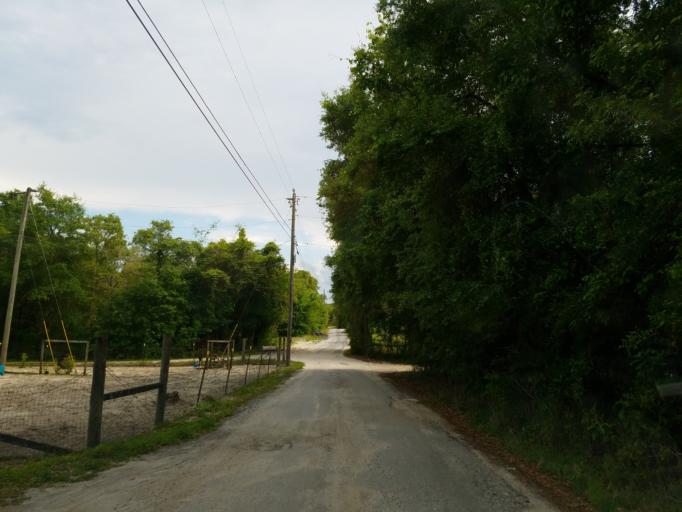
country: US
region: Florida
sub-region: Hernando County
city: Hill 'n Dale
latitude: 28.5321
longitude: -82.2800
